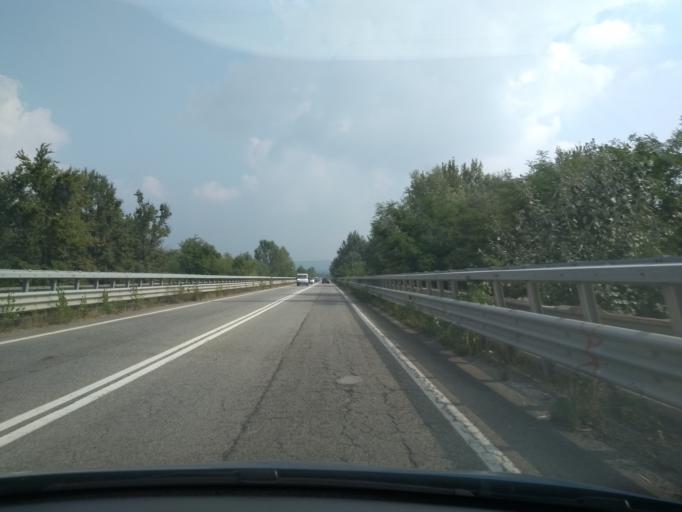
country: IT
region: Piedmont
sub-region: Provincia di Torino
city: Oglianico
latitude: 45.3574
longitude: 7.7070
